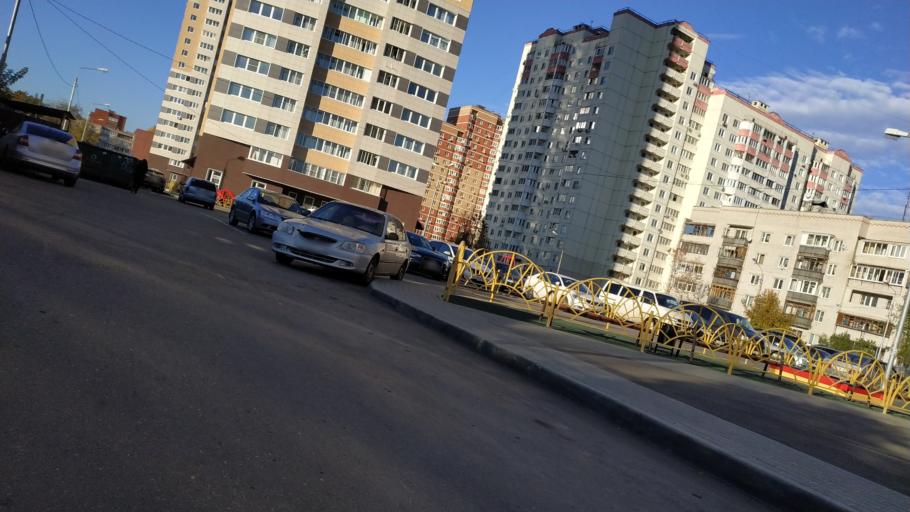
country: RU
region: Moskovskaya
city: Lobnya
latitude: 56.0043
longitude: 37.4648
